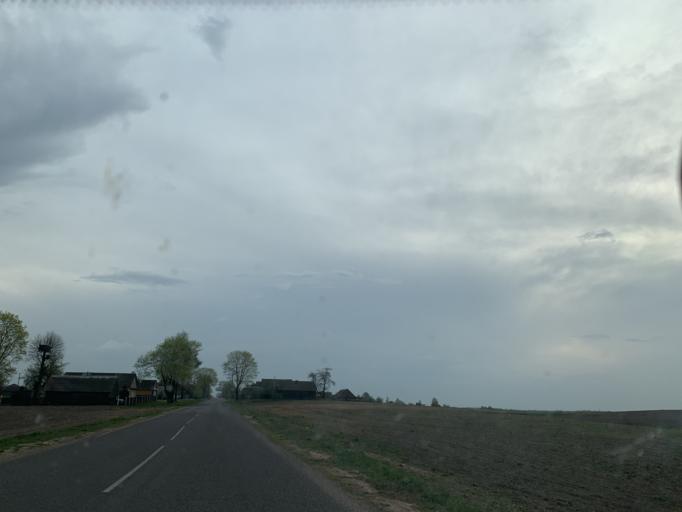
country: BY
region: Minsk
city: Kapyl'
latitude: 53.2862
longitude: 26.9856
